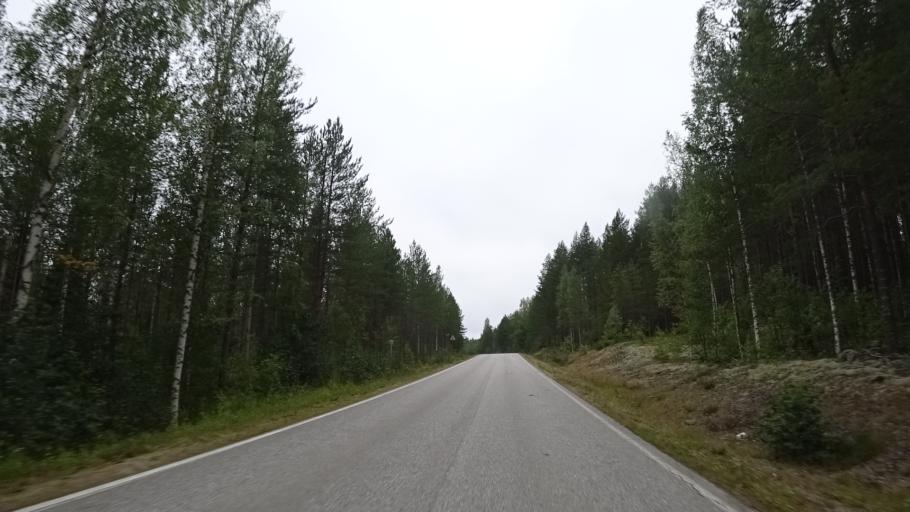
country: FI
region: North Karelia
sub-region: Pielisen Karjala
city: Lieksa
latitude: 63.3257
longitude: 30.2382
